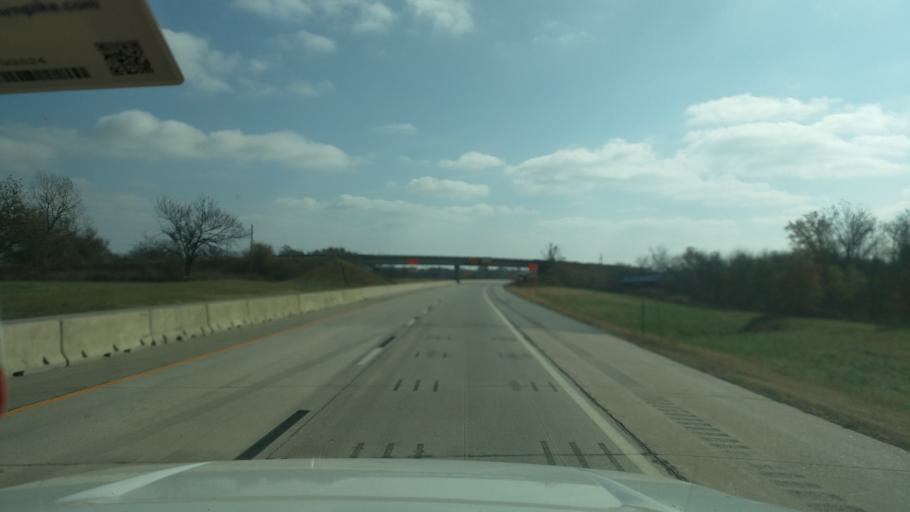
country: US
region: Oklahoma
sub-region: Wagoner County
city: Coweta
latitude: 35.9756
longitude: -95.6029
